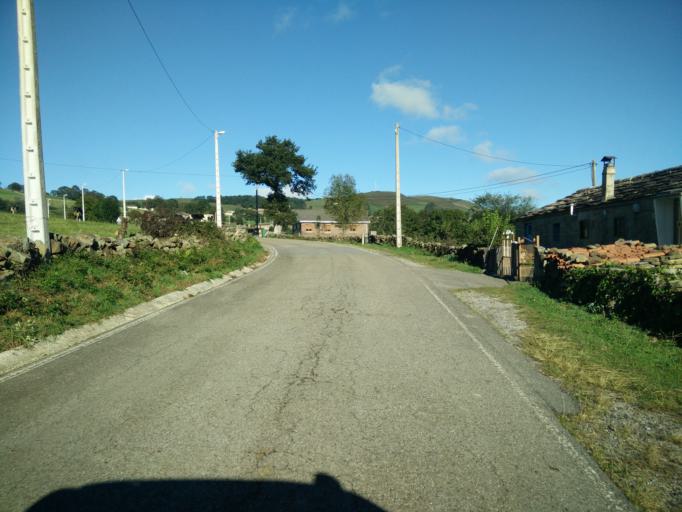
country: ES
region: Cantabria
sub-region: Provincia de Cantabria
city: San Pedro del Romeral
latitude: 43.1093
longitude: -3.8056
